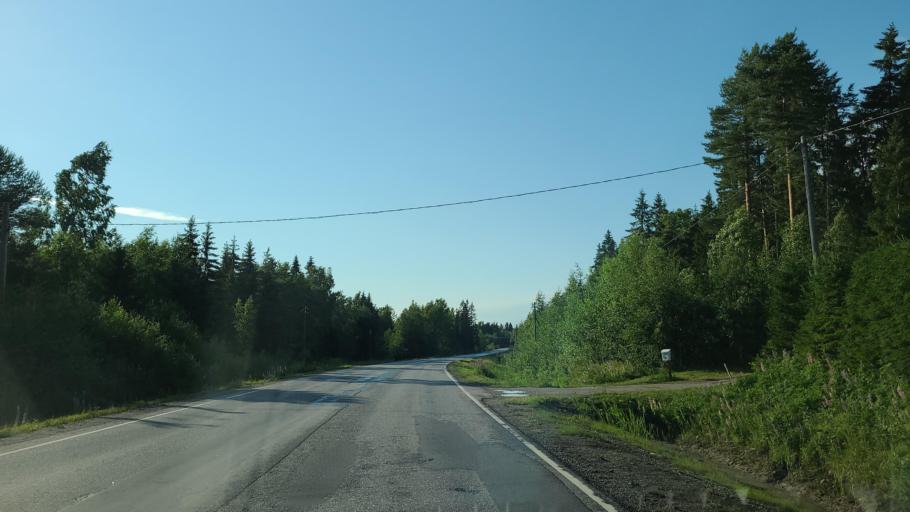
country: FI
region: Ostrobothnia
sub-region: Vaasa
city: Replot
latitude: 63.2105
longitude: 21.4337
